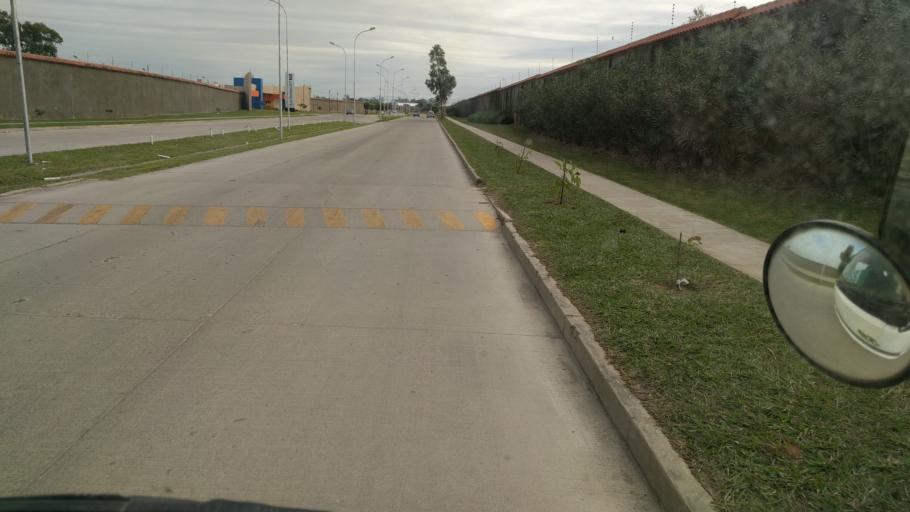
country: BO
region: Santa Cruz
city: Santa Cruz de la Sierra
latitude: -17.6800
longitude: -63.1447
